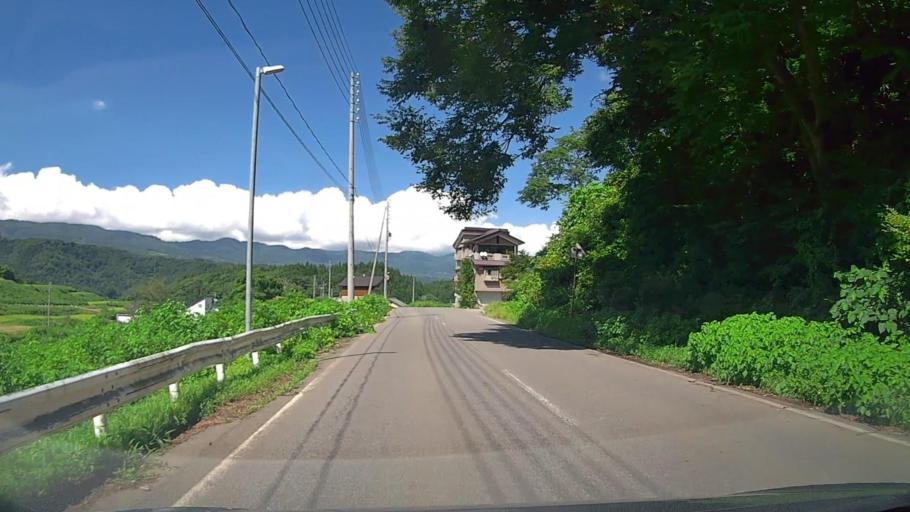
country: JP
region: Nagano
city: Iiyama
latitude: 36.9298
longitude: 138.4232
